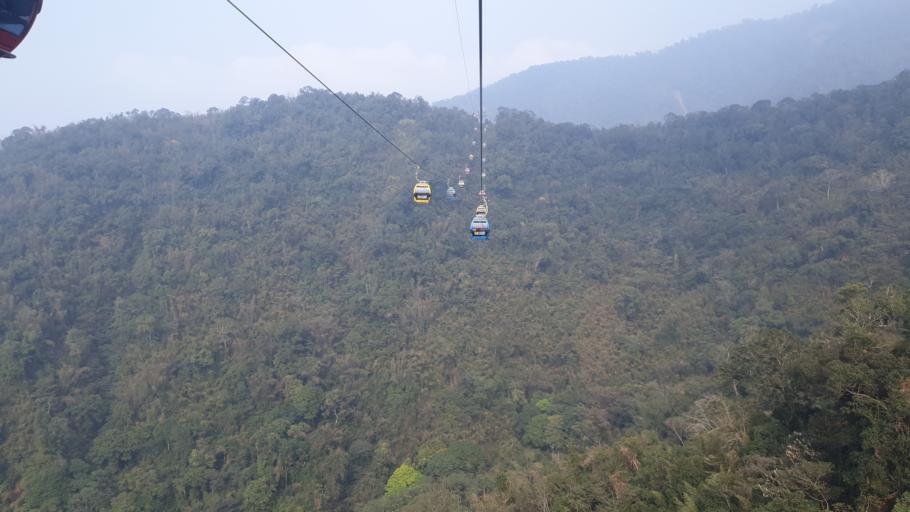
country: TW
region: Taiwan
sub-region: Nantou
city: Puli
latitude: 23.8561
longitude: 120.9428
